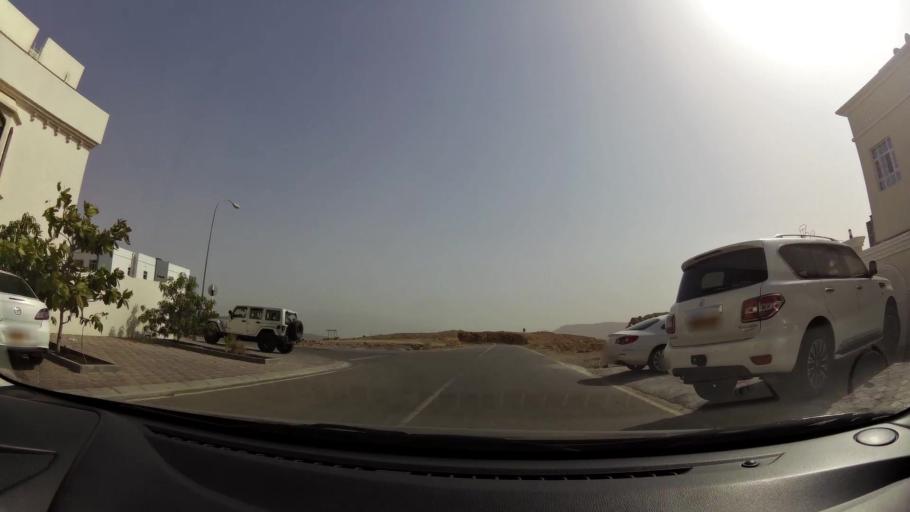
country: OM
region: Muhafazat Masqat
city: Bawshar
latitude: 23.5505
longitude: 58.3483
